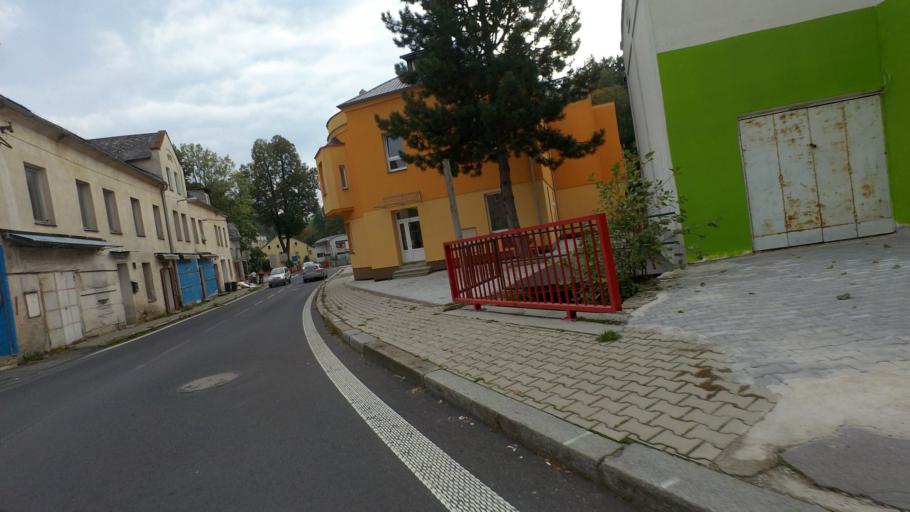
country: CZ
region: Ustecky
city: Dolni Poustevna
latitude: 50.9788
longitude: 14.2890
